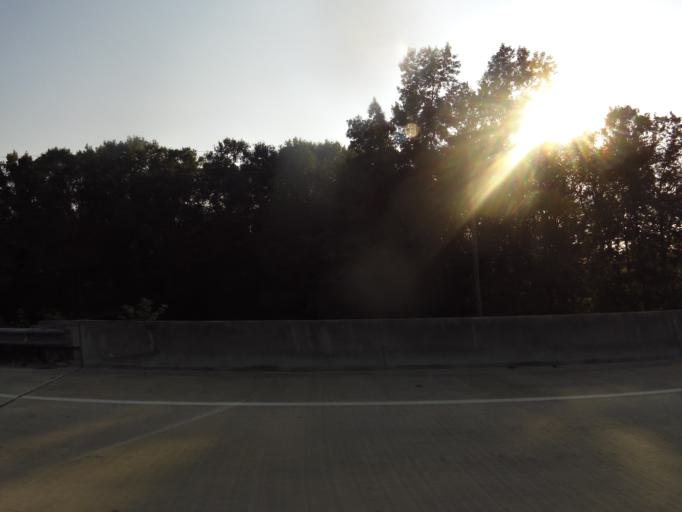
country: US
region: Florida
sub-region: Duval County
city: Baldwin
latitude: 30.3680
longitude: -82.0149
